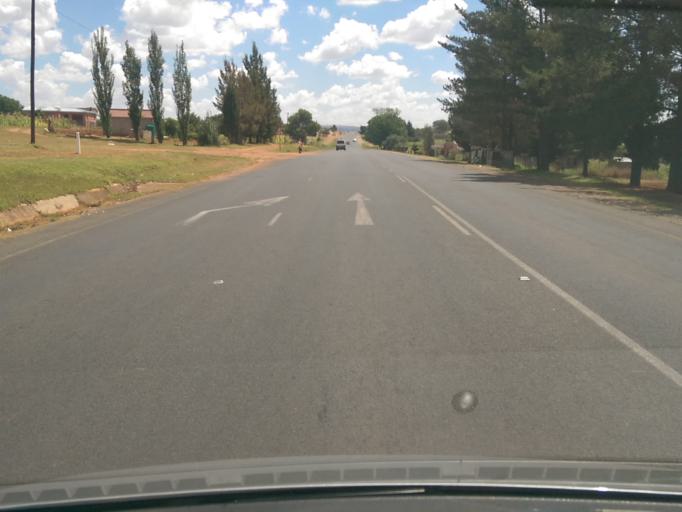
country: LS
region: Maseru
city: Maseru
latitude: -29.4086
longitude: 27.5903
